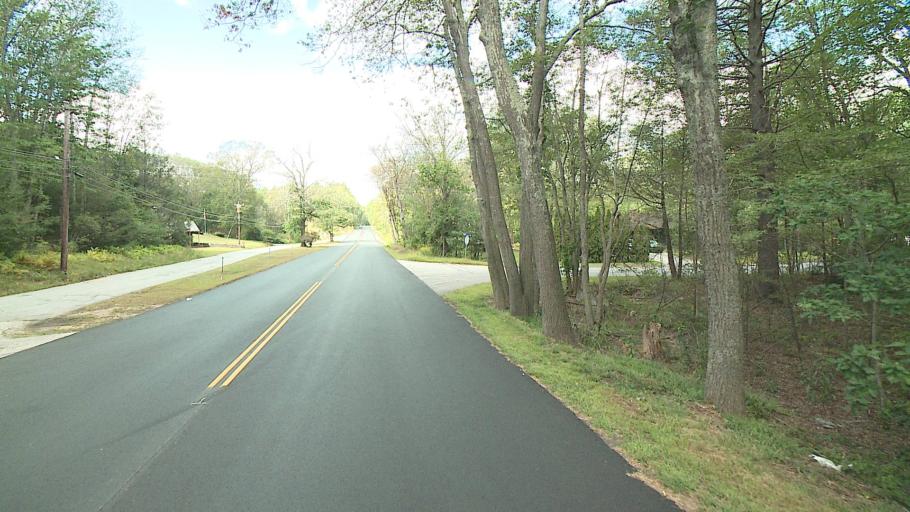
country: US
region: Connecticut
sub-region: Windham County
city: Thompson
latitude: 41.9233
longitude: -71.8446
